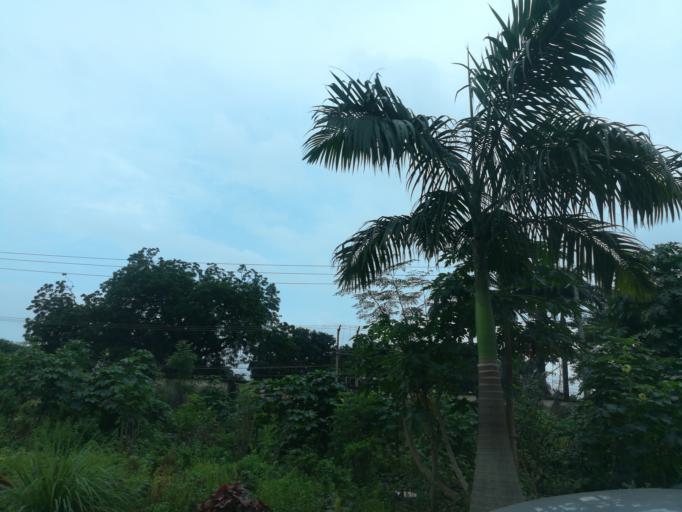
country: NG
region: Lagos
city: Ojota
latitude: 6.5730
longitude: 3.3608
